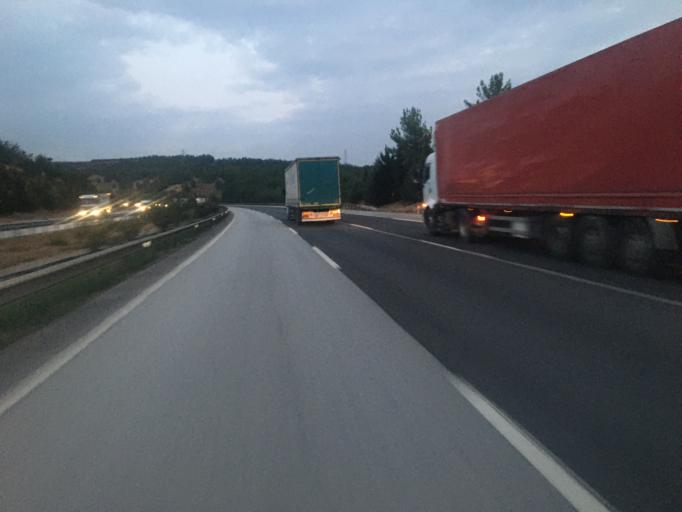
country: TR
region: Osmaniye
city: Haruniye
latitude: 37.1740
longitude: 36.3726
